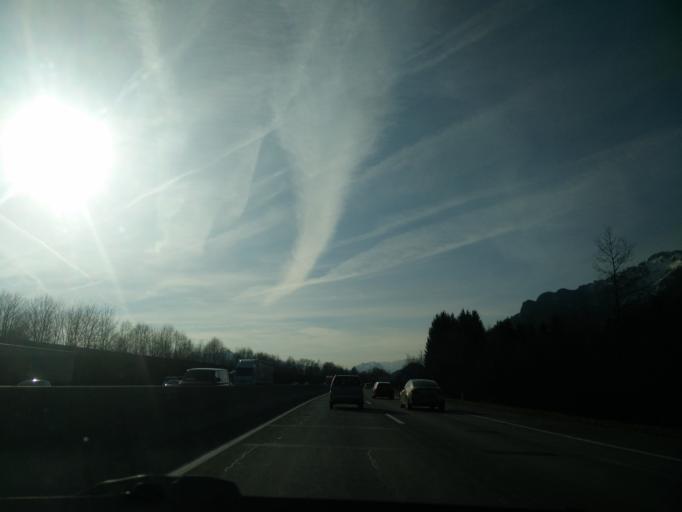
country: AT
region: Salzburg
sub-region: Politischer Bezirk Salzburg-Umgebung
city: Grodig
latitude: 47.7648
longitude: 12.9965
